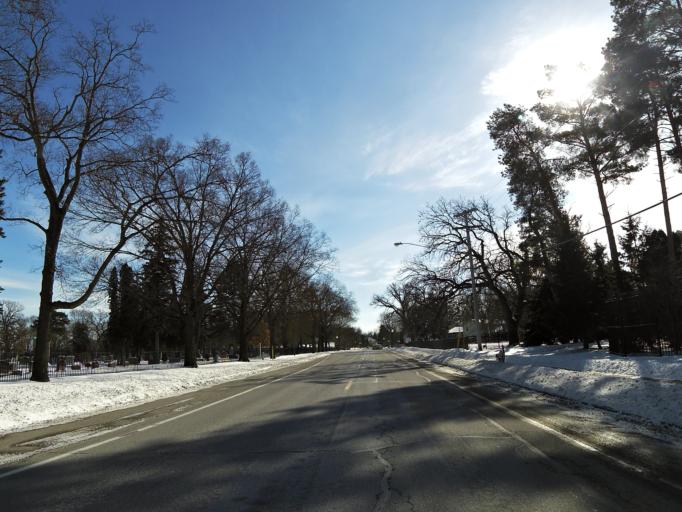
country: US
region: Minnesota
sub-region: Dakota County
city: Hastings
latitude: 44.7466
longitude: -92.8703
